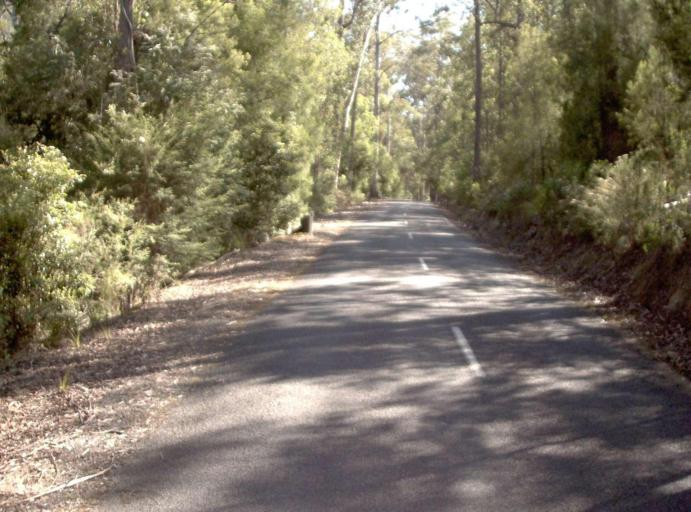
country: AU
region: Victoria
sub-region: East Gippsland
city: Lakes Entrance
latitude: -37.4589
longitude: 148.5694
